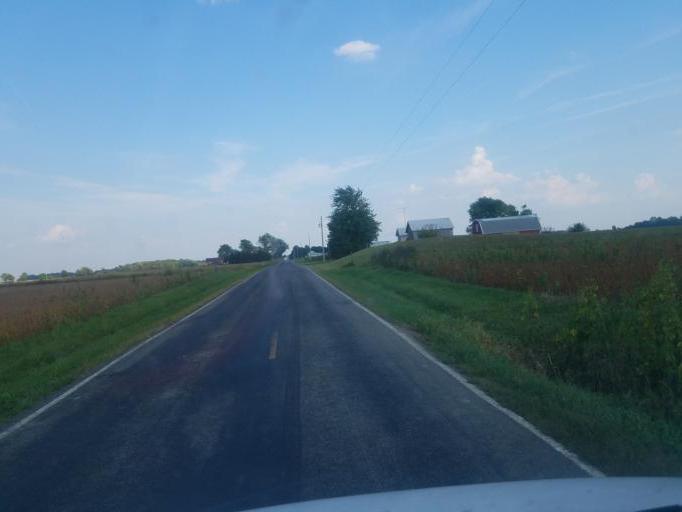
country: US
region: Ohio
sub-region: Hardin County
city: Forest
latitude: 40.9049
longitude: -83.4926
